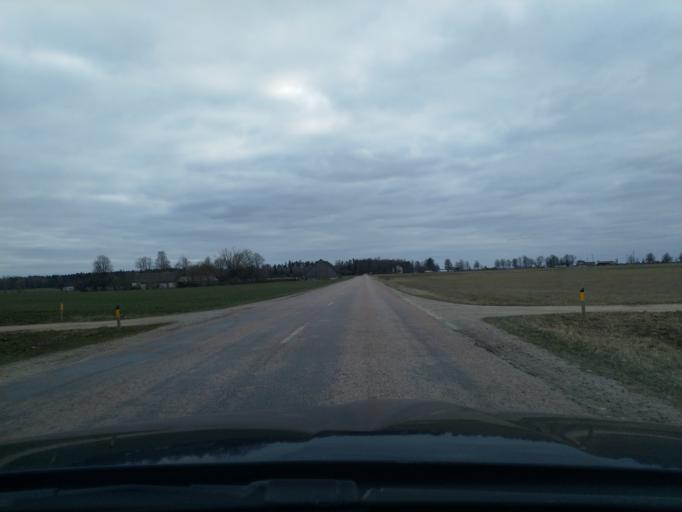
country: LV
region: Talsu Rajons
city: Sabile
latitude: 56.9412
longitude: 22.5956
